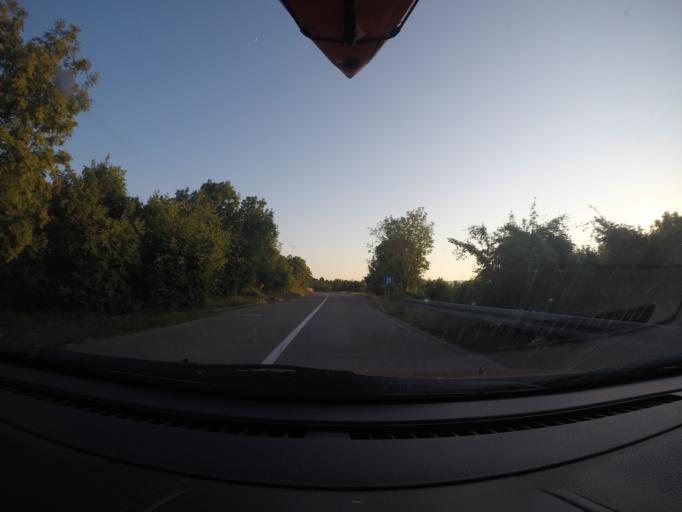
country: RO
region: Mehedinti
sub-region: Comuna Eselnita
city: Eselnita
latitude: 44.6610
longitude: 22.3257
